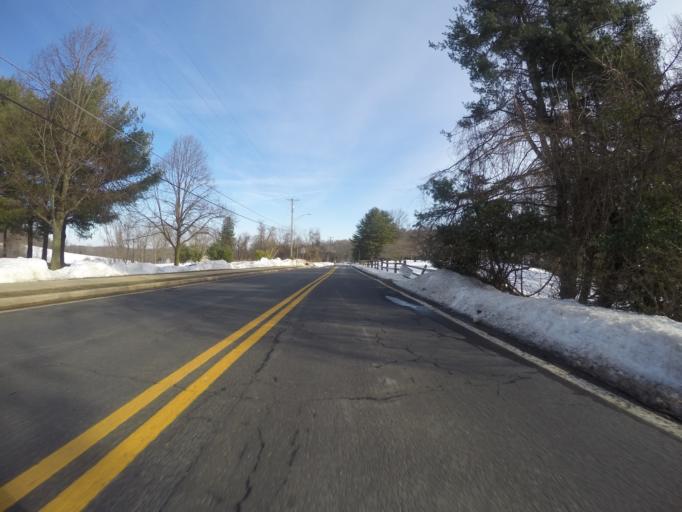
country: US
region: Maryland
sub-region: Baltimore County
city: Hunt Valley
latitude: 39.5715
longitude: -76.6520
